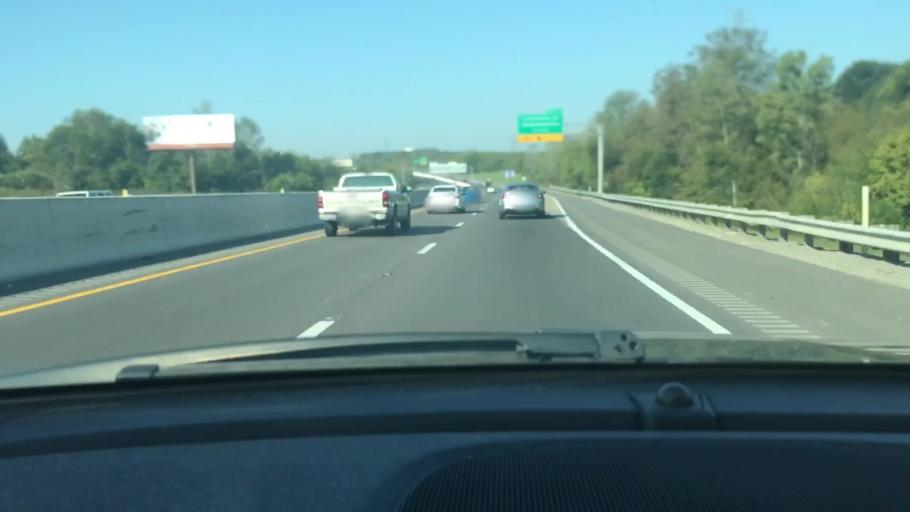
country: US
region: Tennessee
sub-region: Davidson County
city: Goodlettsville
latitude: 36.3123
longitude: -86.6767
